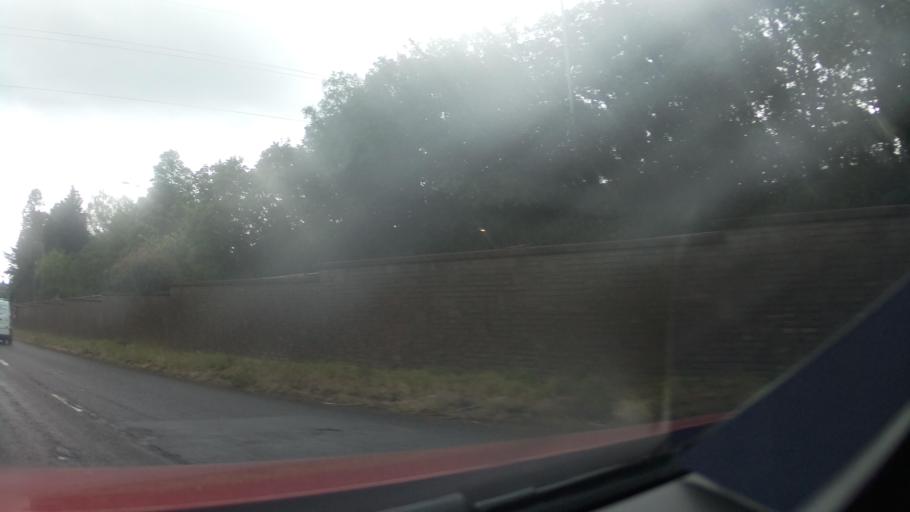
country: GB
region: England
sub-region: Dudley
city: Kingswinford
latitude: 52.5513
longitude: -2.1714
